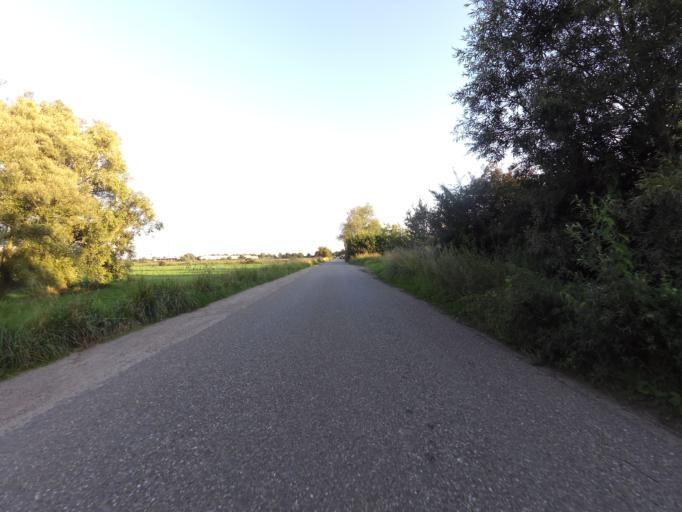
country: NL
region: Gelderland
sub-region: Gemeente Zevenaar
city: Zevenaar
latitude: 51.8804
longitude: 6.0486
